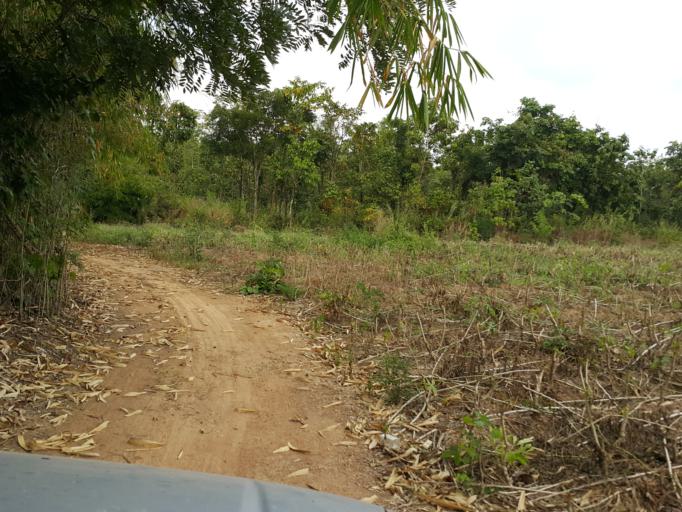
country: TH
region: Sukhothai
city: Thung Saliam
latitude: 17.4022
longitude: 99.5864
